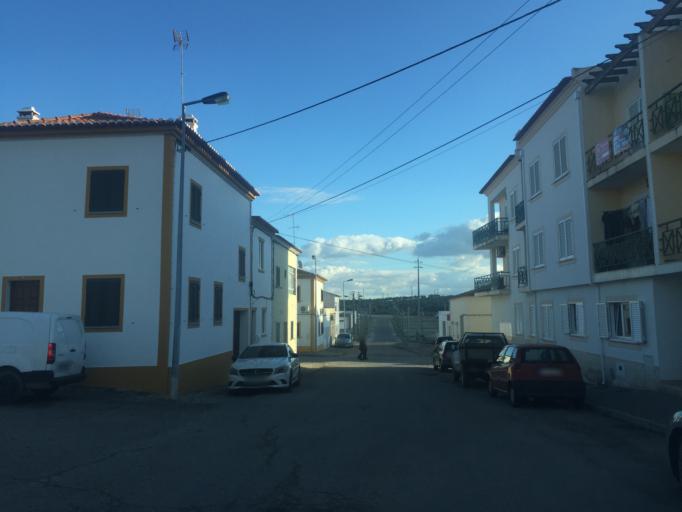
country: PT
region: Portalegre
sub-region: Alter do Chao
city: Alter do Chao
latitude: 39.1963
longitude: -7.6555
